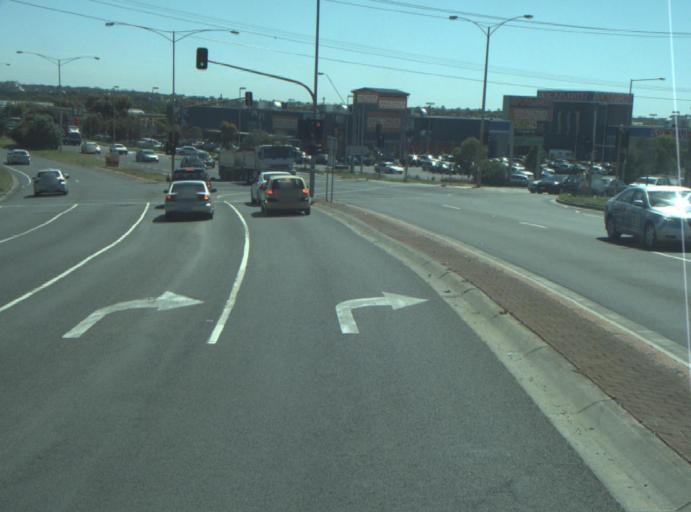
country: AU
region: Victoria
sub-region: Greater Geelong
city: Breakwater
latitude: -38.1811
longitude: 144.3499
